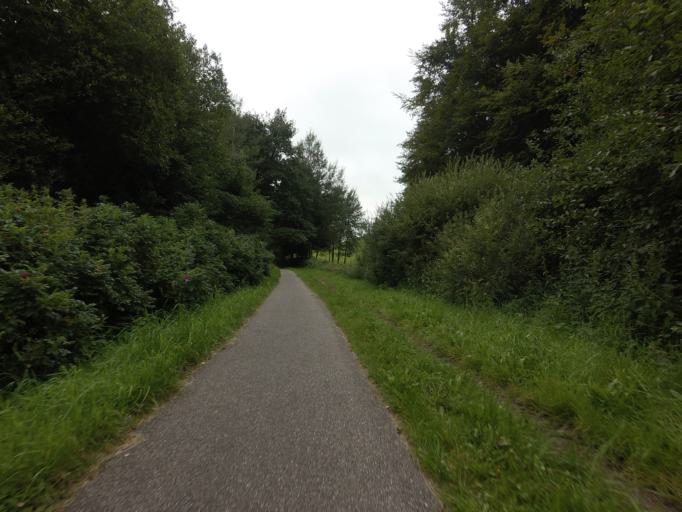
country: DK
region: Central Jutland
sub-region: Silkeborg Kommune
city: Virklund
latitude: 56.1076
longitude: 9.5596
